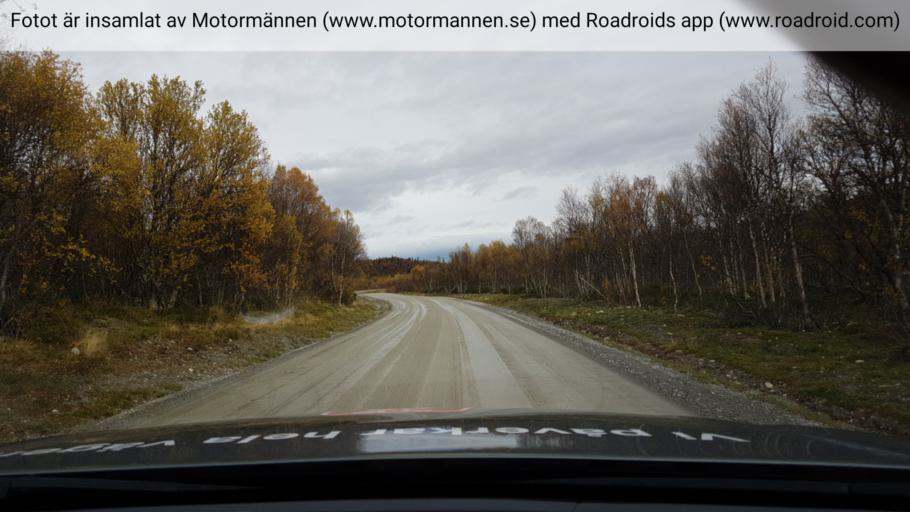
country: SE
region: Jaemtland
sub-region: Are Kommun
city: Are
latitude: 62.5932
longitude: 12.6081
